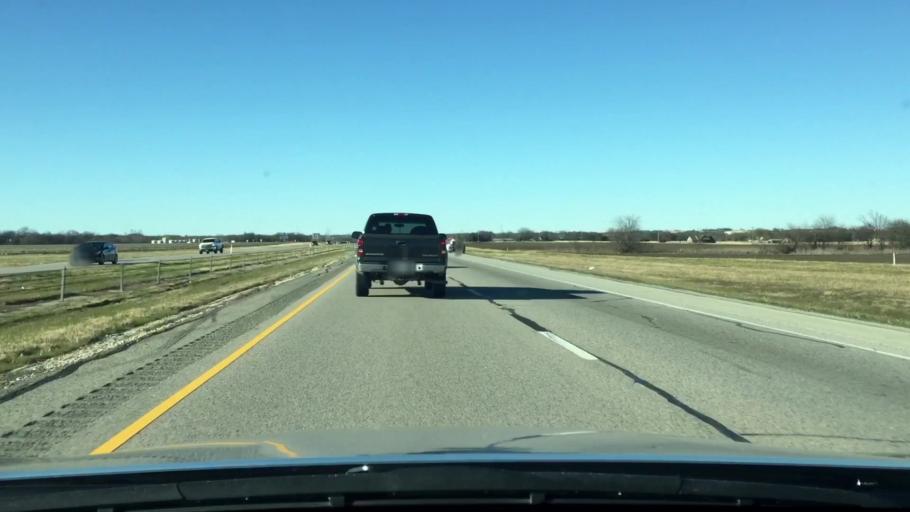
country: US
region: Texas
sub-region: Johnson County
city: Grandview
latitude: 32.2795
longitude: -97.1739
